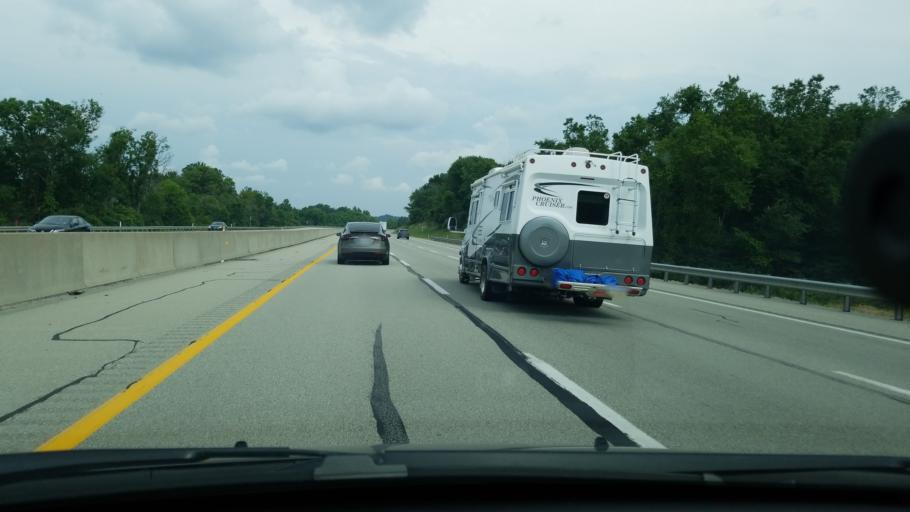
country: US
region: Pennsylvania
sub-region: Lawrence County
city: New Beaver
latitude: 40.8872
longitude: -80.4366
